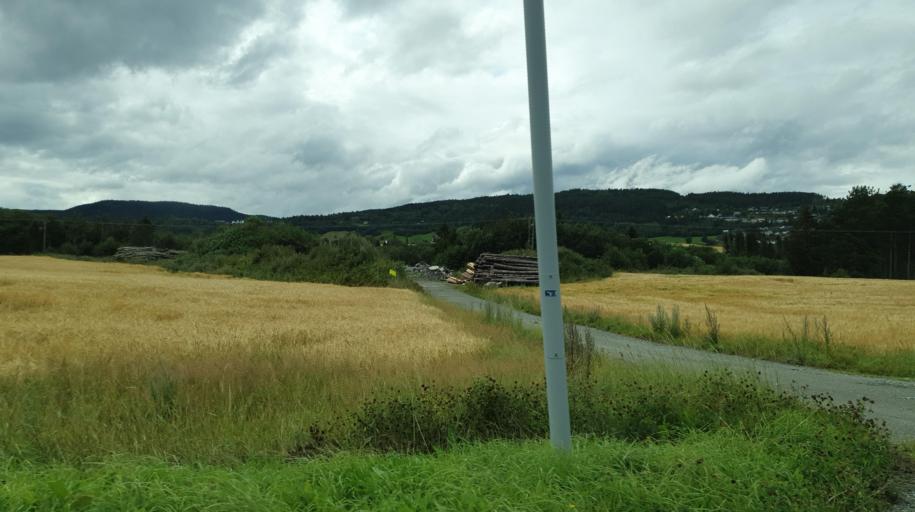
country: NO
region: Nord-Trondelag
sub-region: Stjordal
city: Stjordalshalsen
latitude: 63.4399
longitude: 10.9411
